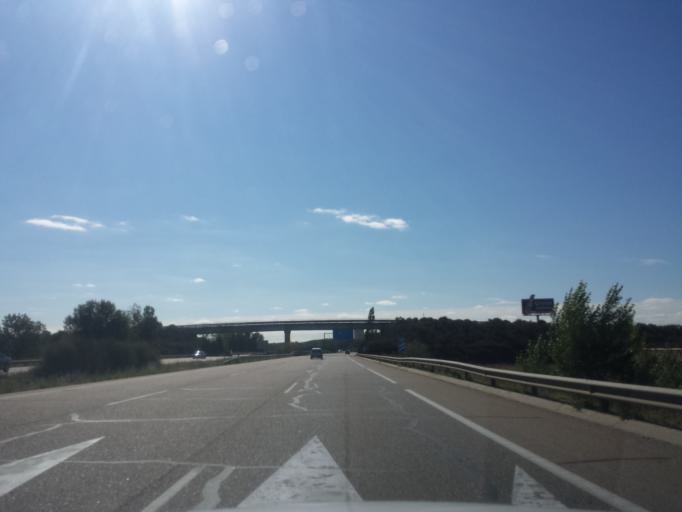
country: ES
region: Castille and Leon
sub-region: Provincia de Zamora
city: Villanueva de Azoague
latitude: 41.9937
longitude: -5.6438
